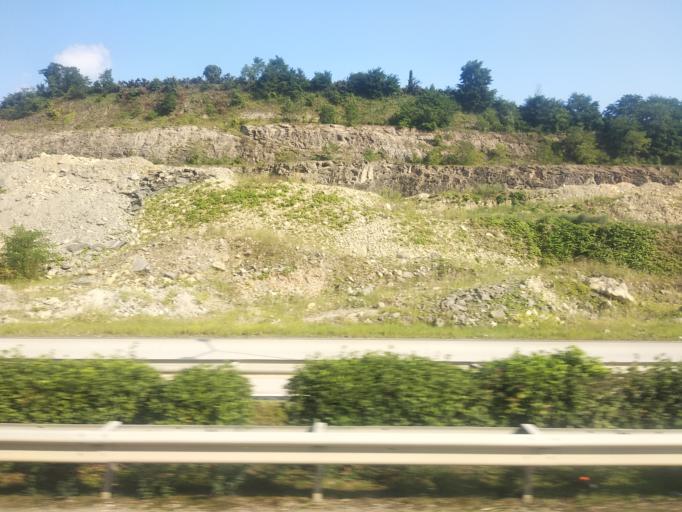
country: TR
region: Ordu
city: Ordu
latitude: 40.9977
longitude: 37.8203
